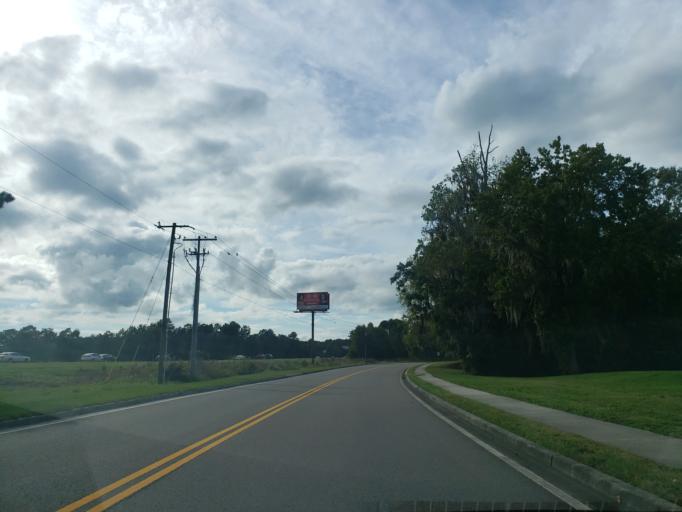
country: US
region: Georgia
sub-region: Chatham County
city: Georgetown
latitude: 32.0022
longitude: -81.2601
